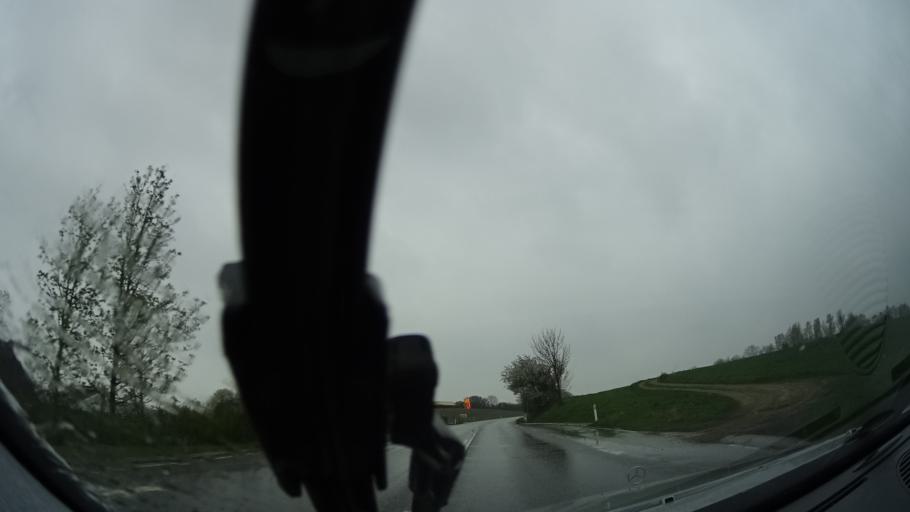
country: DK
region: Zealand
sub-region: Odsherred Kommune
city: Asnaes
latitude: 55.7958
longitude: 11.6023
